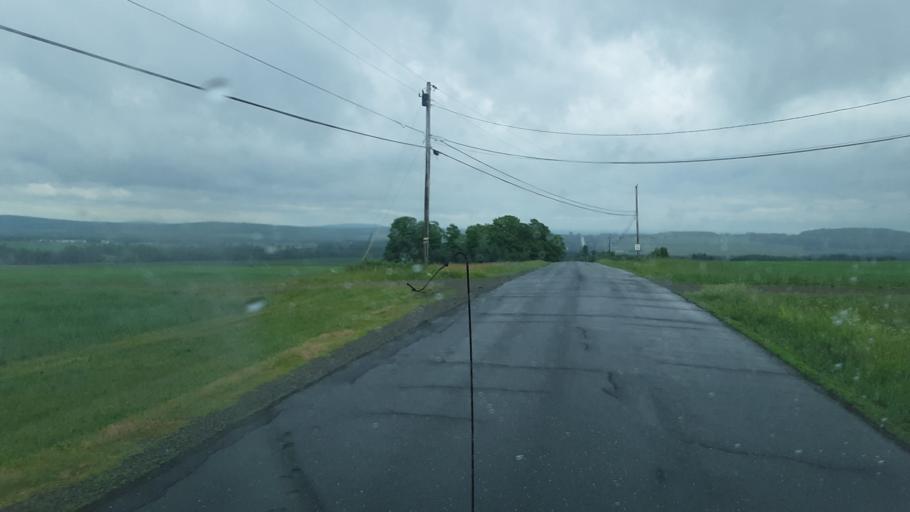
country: US
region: Maine
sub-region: Aroostook County
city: Presque Isle
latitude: 46.6818
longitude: -68.1846
